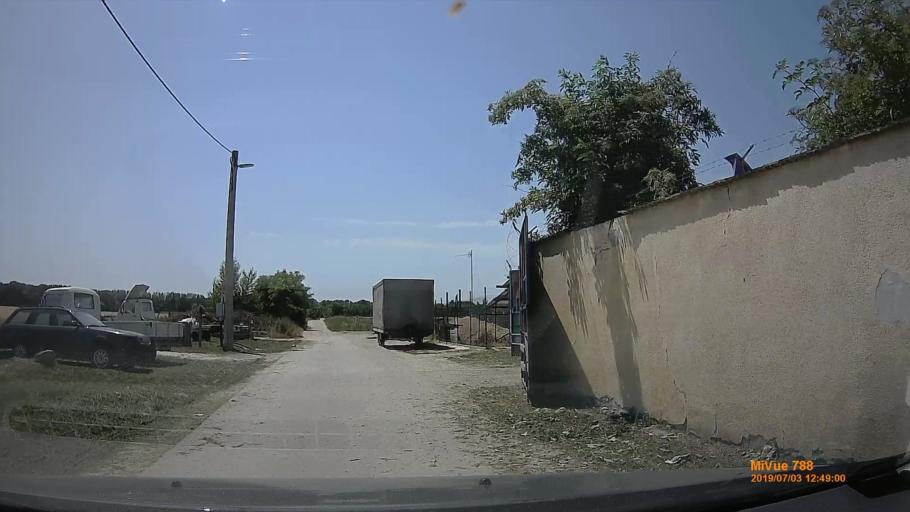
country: HU
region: Gyor-Moson-Sopron
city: Gyor
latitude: 47.7160
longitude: 17.6023
